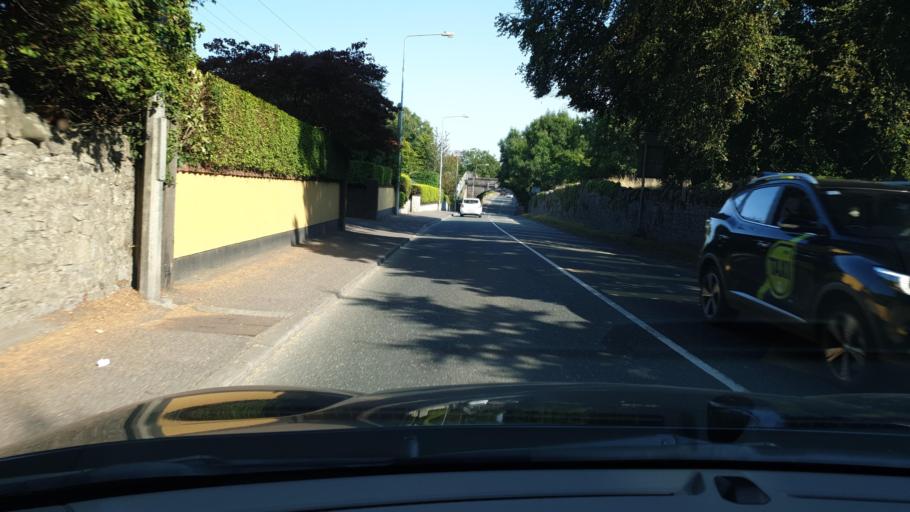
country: IE
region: Leinster
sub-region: An Mhi
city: Navan
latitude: 53.6528
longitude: -6.6749
